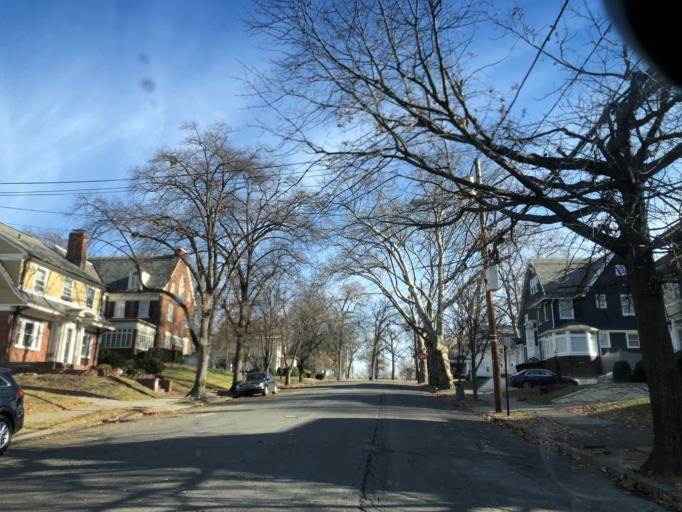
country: US
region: New Jersey
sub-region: Bergen County
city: Elmwood Park
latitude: 40.9157
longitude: -74.1409
